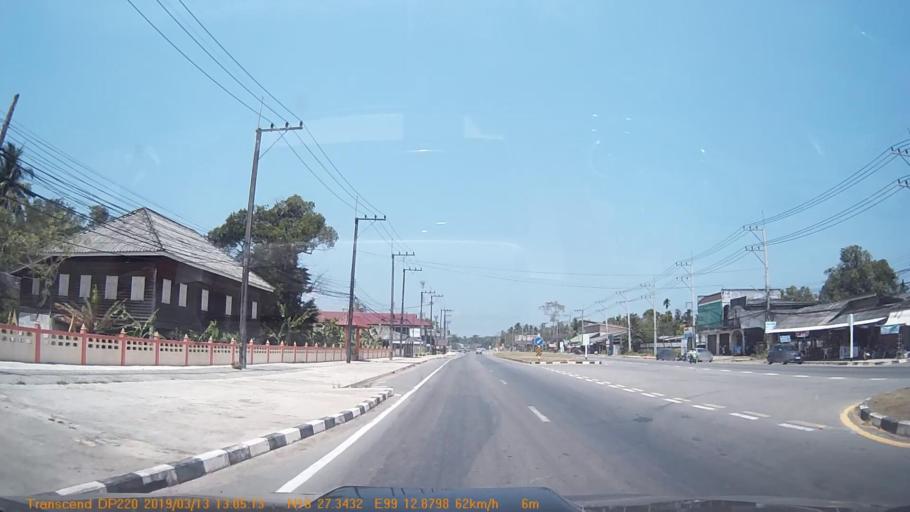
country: TH
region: Chumphon
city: Chumphon
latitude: 10.4562
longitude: 99.2148
